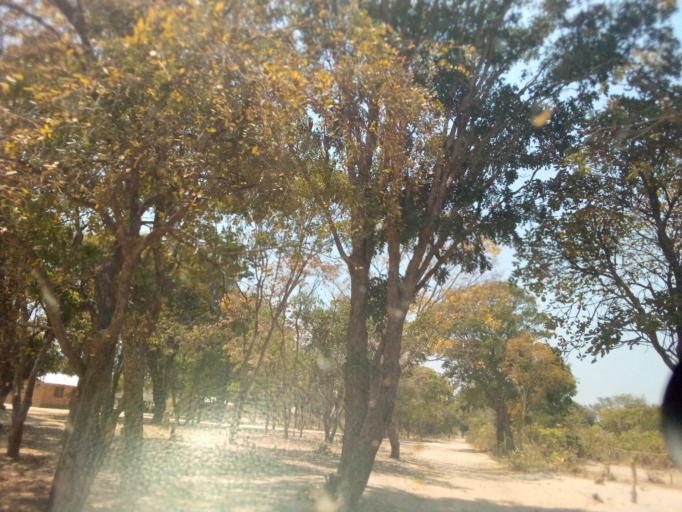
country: ZM
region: Copperbelt
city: Kataba
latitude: -12.2553
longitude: 30.3568
